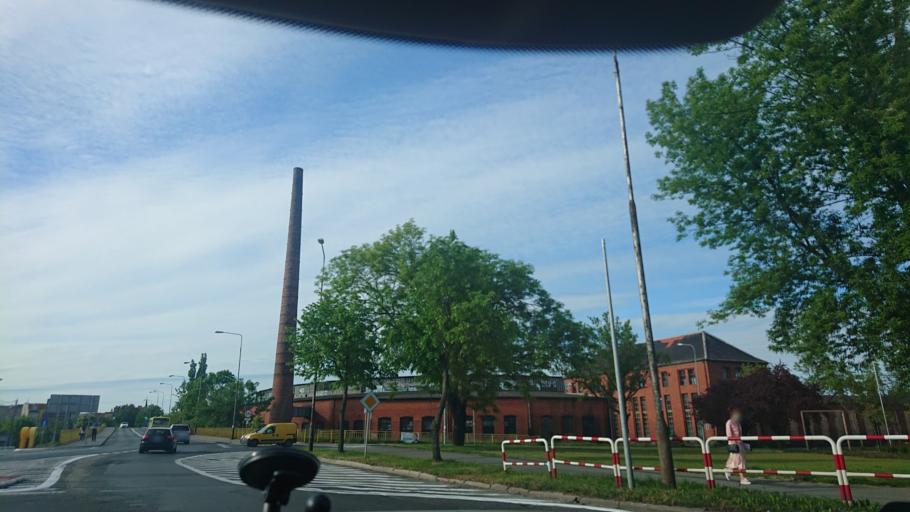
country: PL
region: Greater Poland Voivodeship
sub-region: Powiat gnieznienski
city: Gniezno
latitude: 52.5269
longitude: 17.5975
